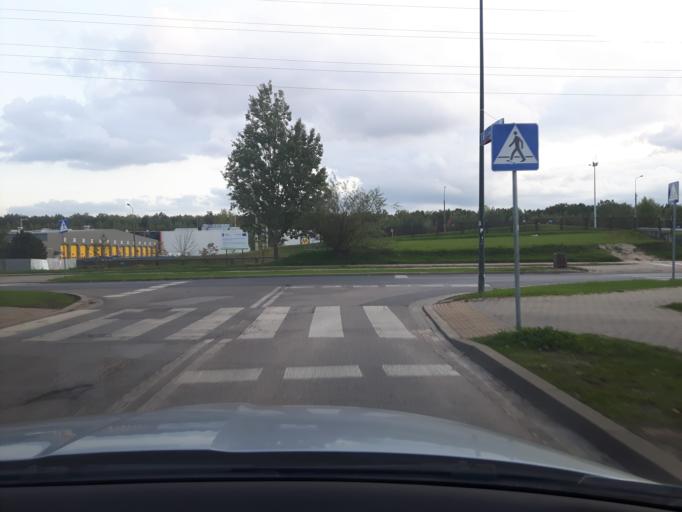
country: PL
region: Masovian Voivodeship
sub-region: Warszawa
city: Kabaty
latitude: 52.1273
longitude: 21.0693
